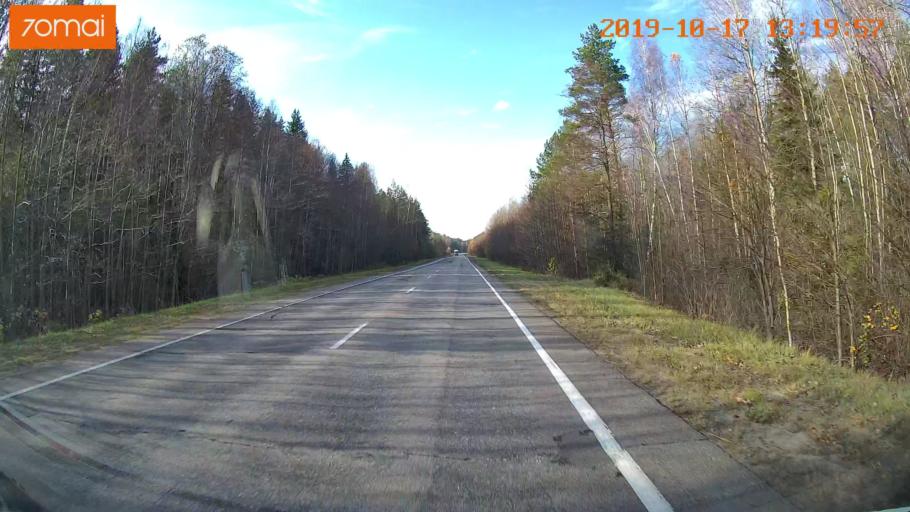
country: RU
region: Rjazan
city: Gus'-Zheleznyy
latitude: 55.0727
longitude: 41.0619
